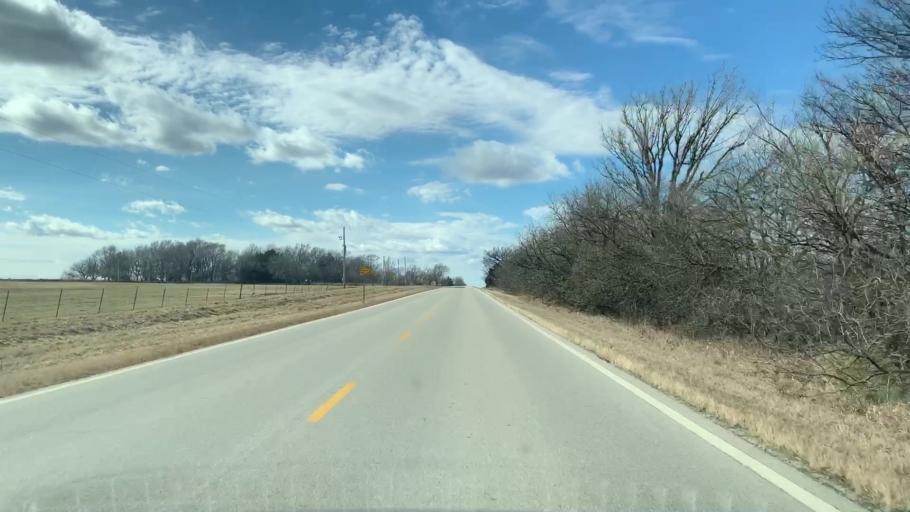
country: US
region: Kansas
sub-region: Neosho County
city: Chanute
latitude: 37.5288
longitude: -95.4400
